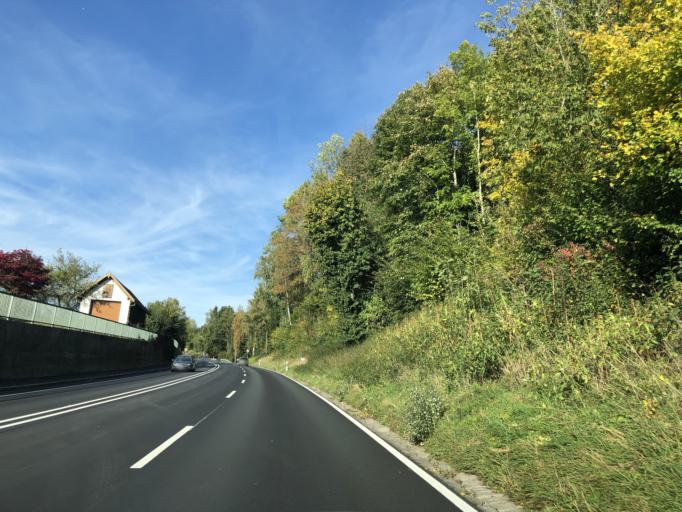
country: DE
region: Bavaria
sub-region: Lower Bavaria
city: Grafling
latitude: 48.8935
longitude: 12.9784
